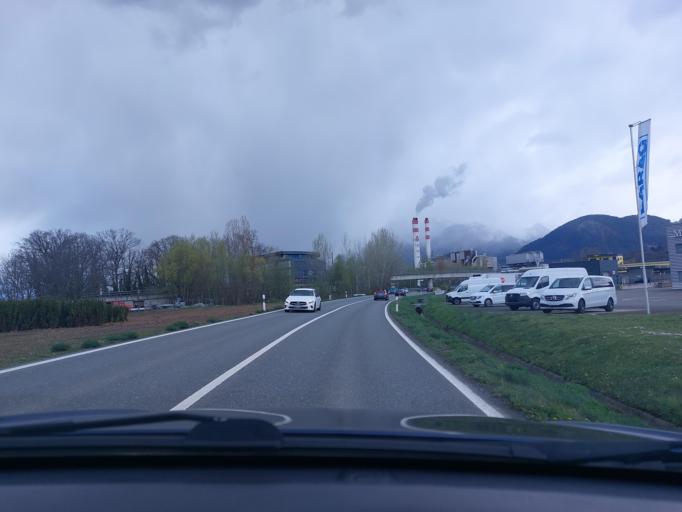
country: CH
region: Valais
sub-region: Monthey District
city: Collombey
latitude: 46.2730
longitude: 6.9577
